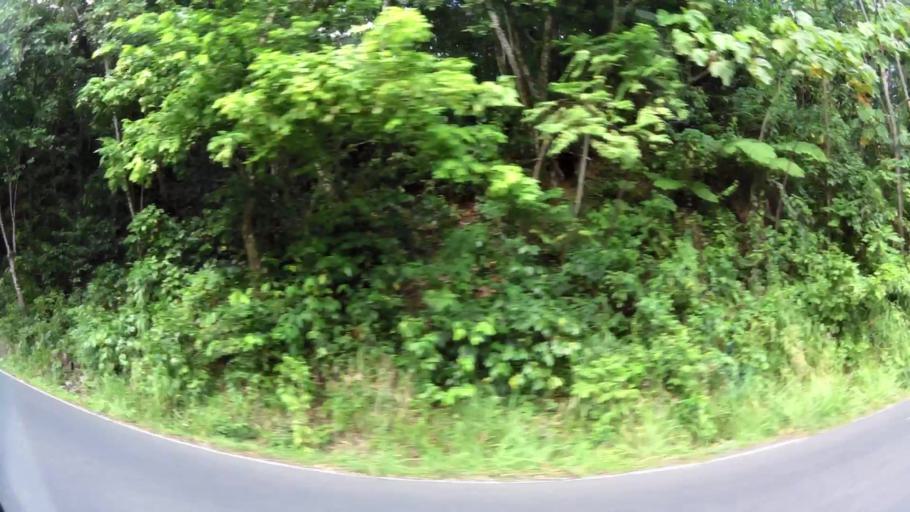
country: LC
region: Dennery Quarter
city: Dennery
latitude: 13.9278
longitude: -60.9440
